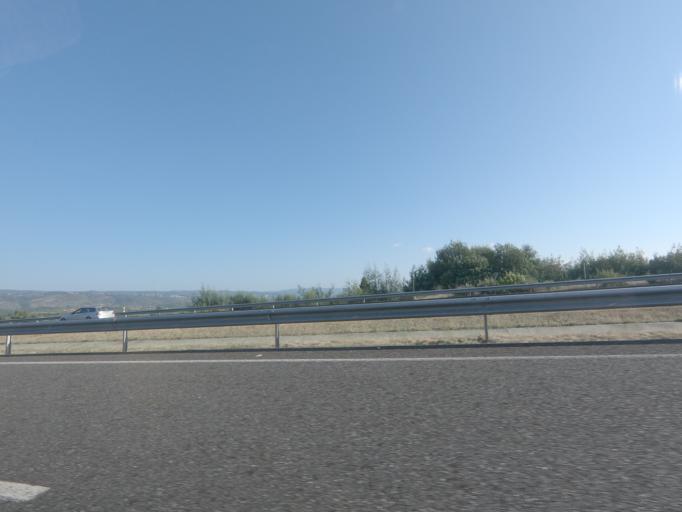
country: ES
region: Galicia
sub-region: Provincia de Ourense
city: Oimbra
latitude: 41.8538
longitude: -7.4181
